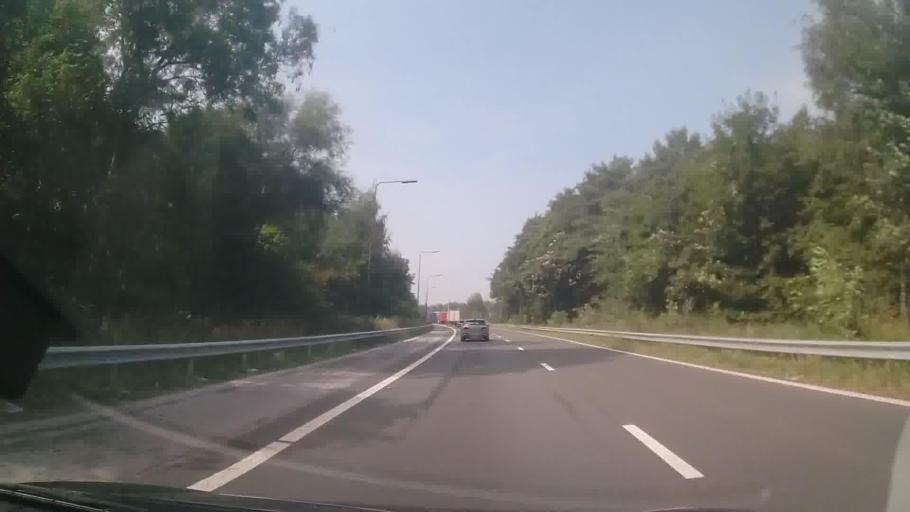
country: GB
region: England
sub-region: Warrington
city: Croft
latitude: 53.4248
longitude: -2.5585
